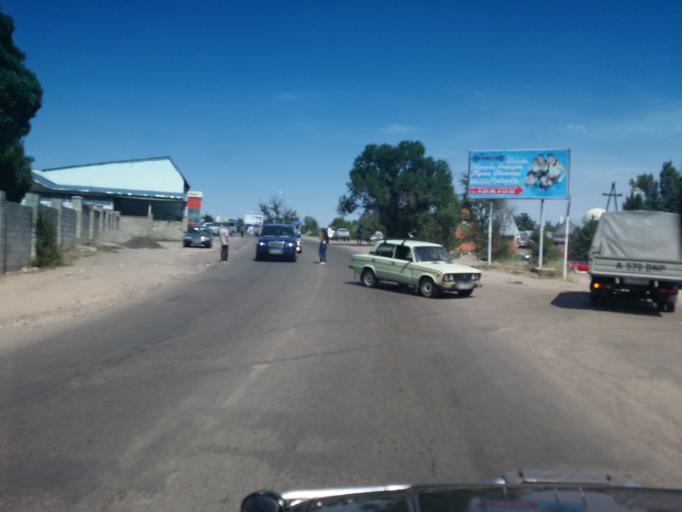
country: KZ
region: Almaty Oblysy
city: Esik
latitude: 43.3516
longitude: 77.4607
